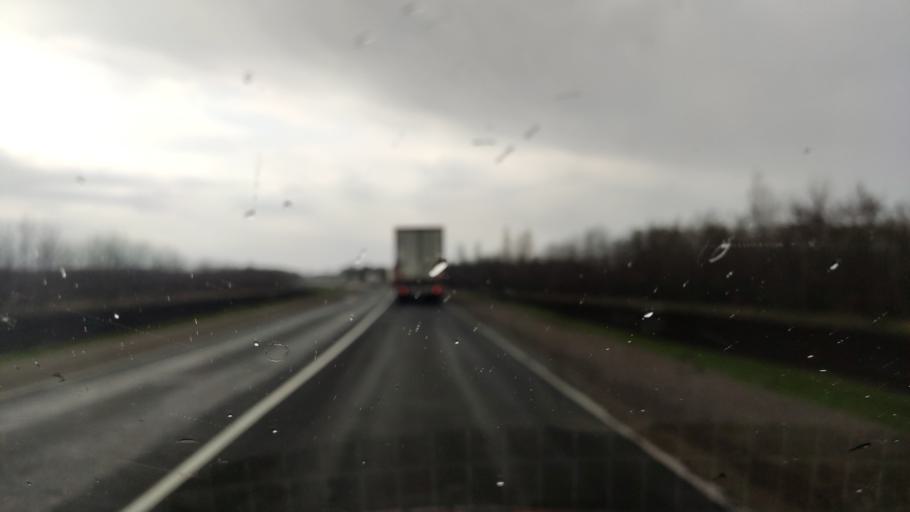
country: RU
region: Voronezj
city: Nizhnedevitsk
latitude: 51.5730
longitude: 38.3299
